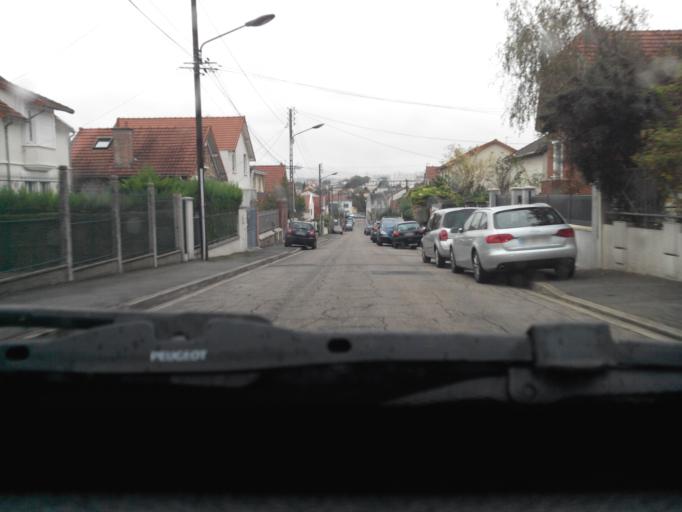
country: FR
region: Ile-de-France
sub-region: Departement du Val-de-Marne
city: L'Hay-les-Roses
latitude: 48.7815
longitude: 2.3307
